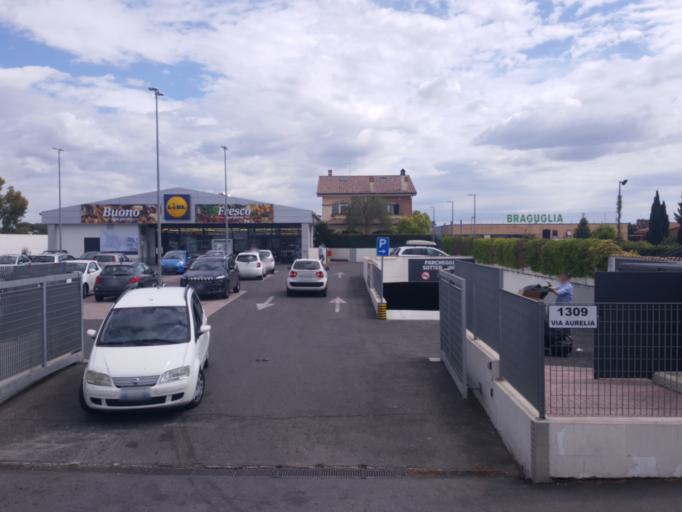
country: IT
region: Latium
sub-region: Citta metropolitana di Roma Capitale
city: La Massimina-Casal Lumbroso
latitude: 41.8819
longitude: 12.3533
